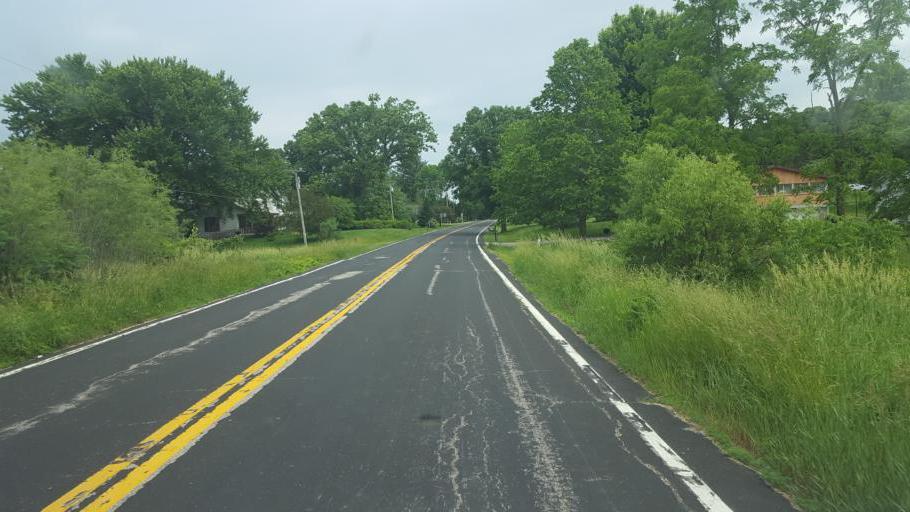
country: US
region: Wisconsin
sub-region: Monroe County
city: Cashton
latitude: 43.7180
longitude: -90.5856
